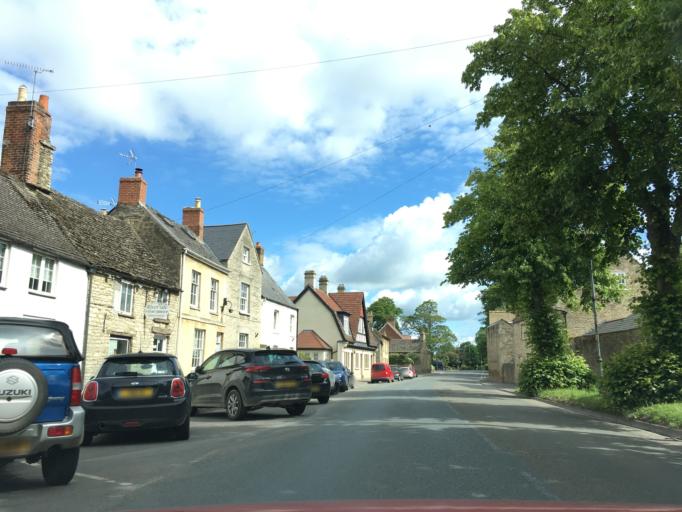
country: GB
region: England
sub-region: Gloucestershire
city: Lechlade
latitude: 51.6962
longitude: -1.6917
